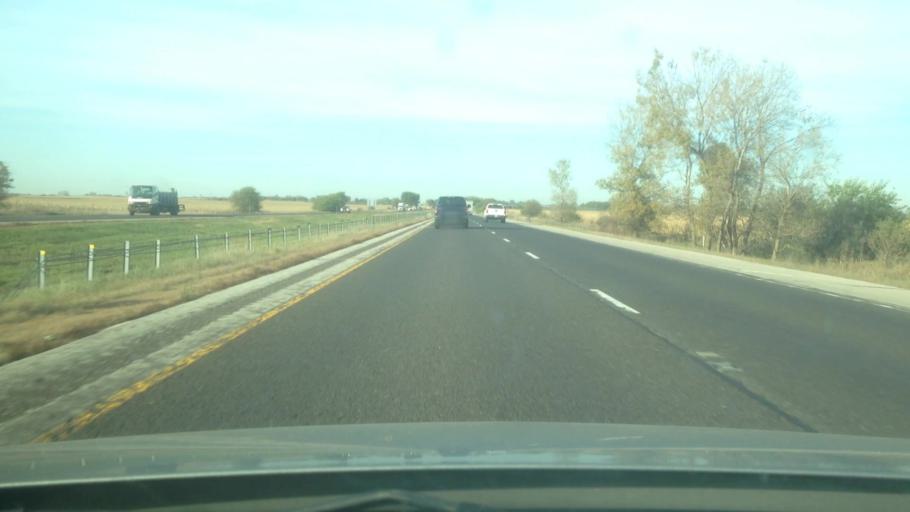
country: US
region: Illinois
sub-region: Will County
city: Peotone
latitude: 41.3375
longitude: -87.8171
